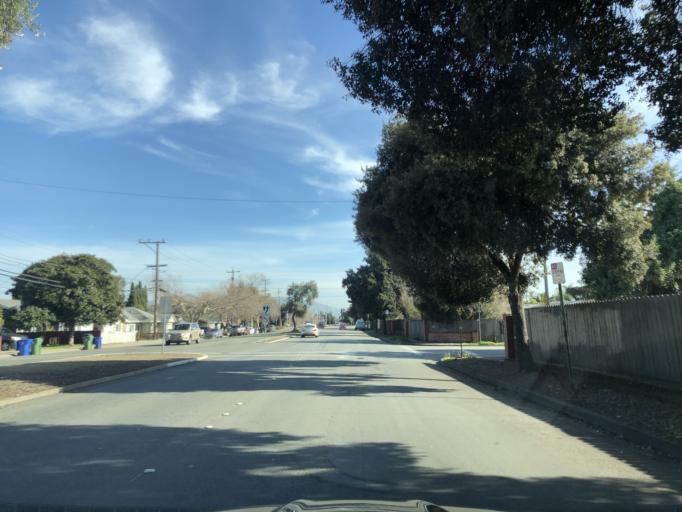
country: US
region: California
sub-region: Alameda County
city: Newark
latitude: 37.5471
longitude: -122.0195
